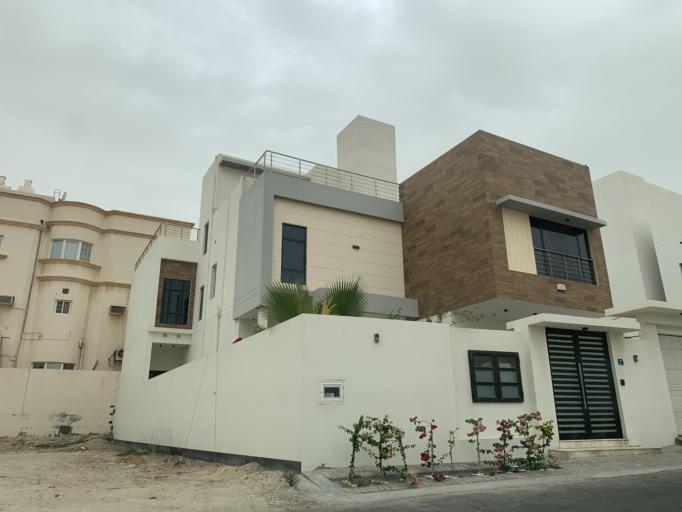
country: BH
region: Central Governorate
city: Madinat Hamad
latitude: 26.1463
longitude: 50.5222
